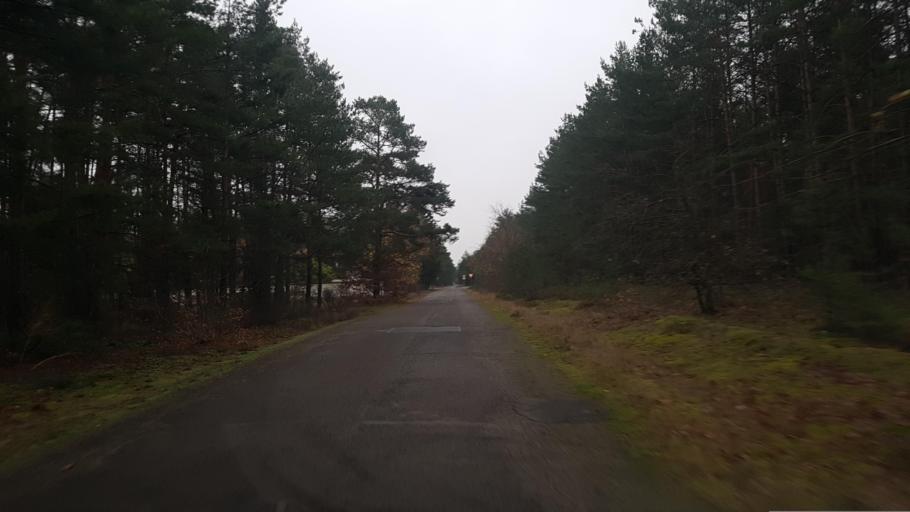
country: DE
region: Brandenburg
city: Ruhland
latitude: 51.4303
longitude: 13.8764
